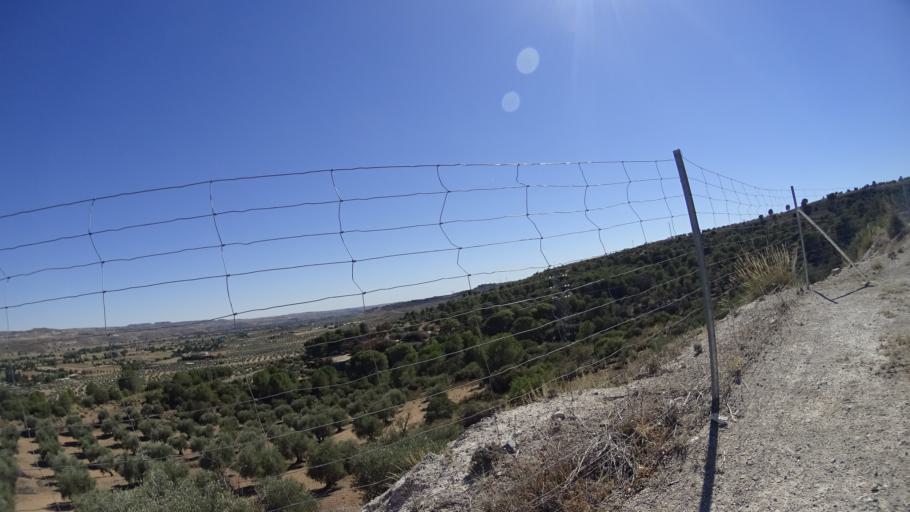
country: ES
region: Madrid
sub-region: Provincia de Madrid
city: Morata de Tajuna
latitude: 40.2308
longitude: -3.4623
